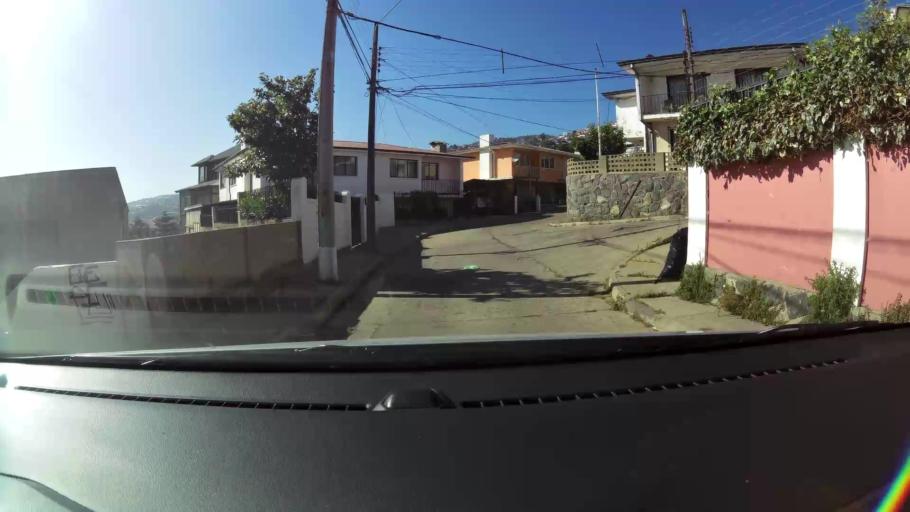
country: CL
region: Valparaiso
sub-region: Provincia de Valparaiso
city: Valparaiso
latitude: -33.0472
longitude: -71.6334
